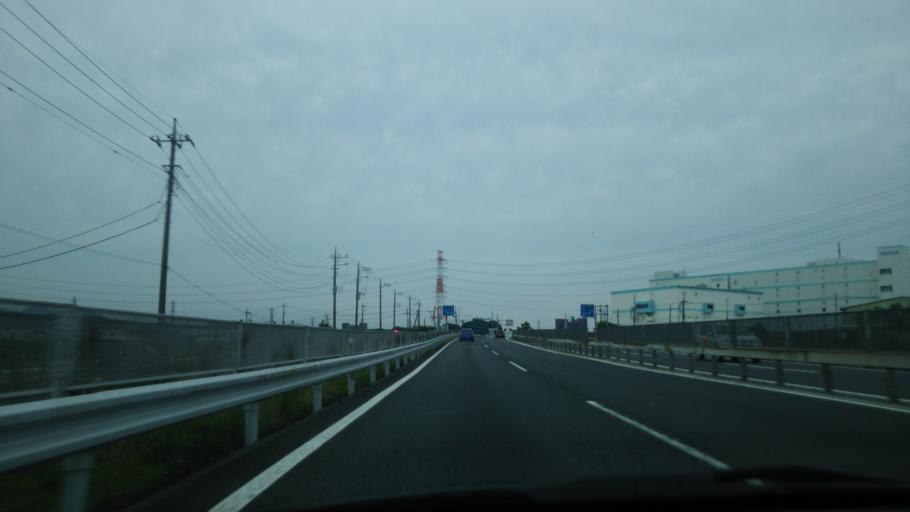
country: JP
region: Kanagawa
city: Isehara
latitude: 35.4005
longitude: 139.3350
